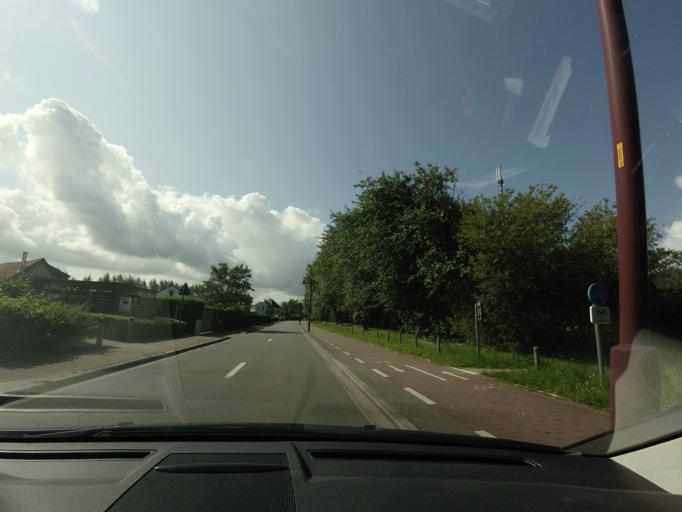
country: BE
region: Flanders
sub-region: Provincie West-Vlaanderen
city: Bredene
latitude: 51.2598
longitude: 2.9950
